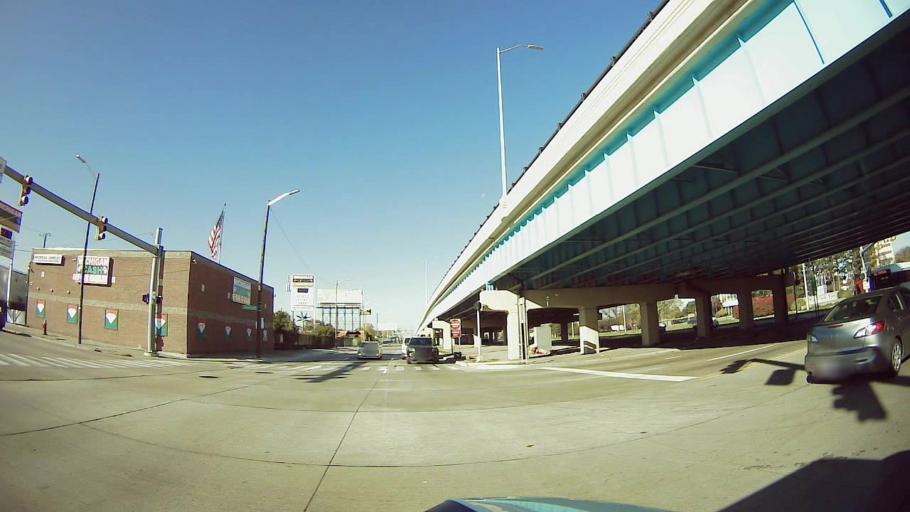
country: US
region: Michigan
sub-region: Oakland County
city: Oak Park
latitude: 42.4448
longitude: -83.2004
